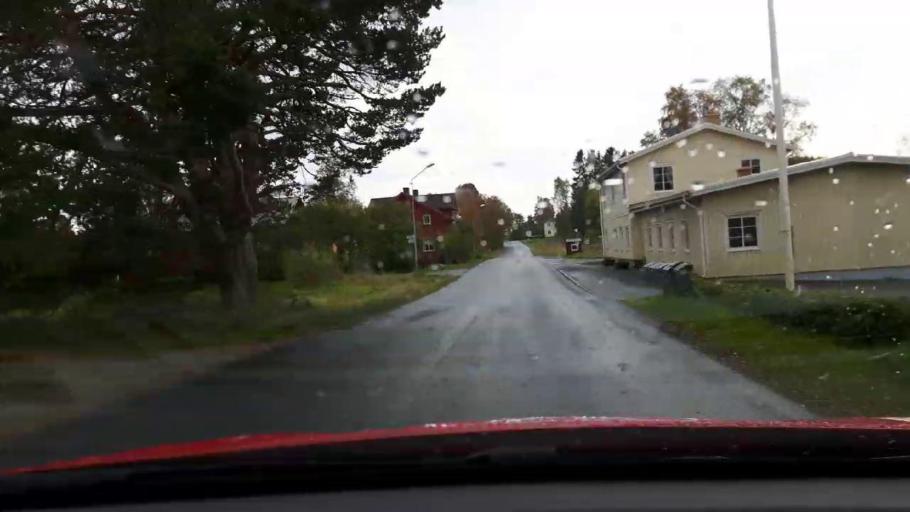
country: SE
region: Jaemtland
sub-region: Bergs Kommun
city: Hoverberg
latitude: 62.9262
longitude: 14.5160
